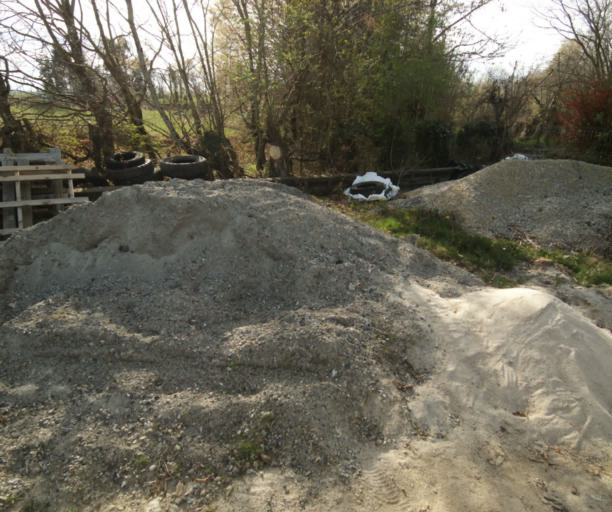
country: FR
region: Limousin
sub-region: Departement de la Correze
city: Naves
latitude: 45.3028
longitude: 1.7361
